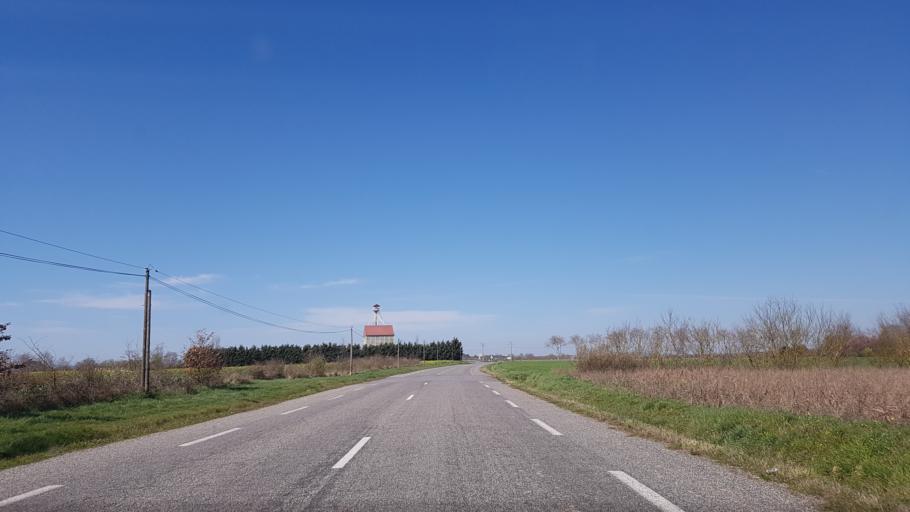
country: FR
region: Midi-Pyrenees
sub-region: Departement de l'Ariege
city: Mazeres
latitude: 43.2331
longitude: 1.6605
